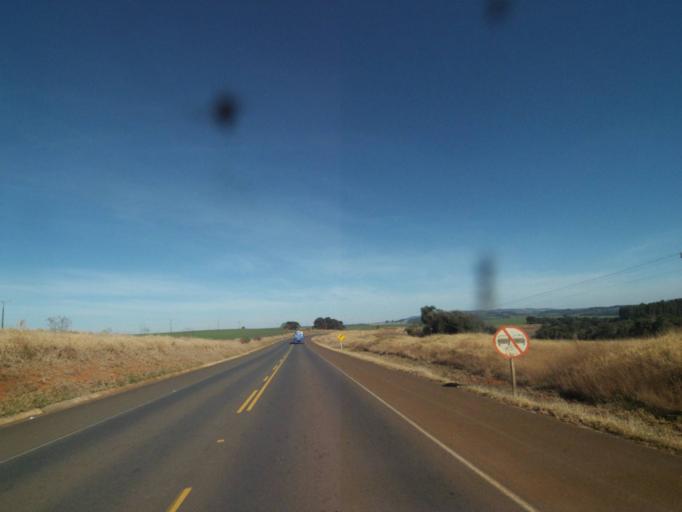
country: BR
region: Parana
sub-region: Tibagi
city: Tibagi
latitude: -24.4539
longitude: -50.4237
